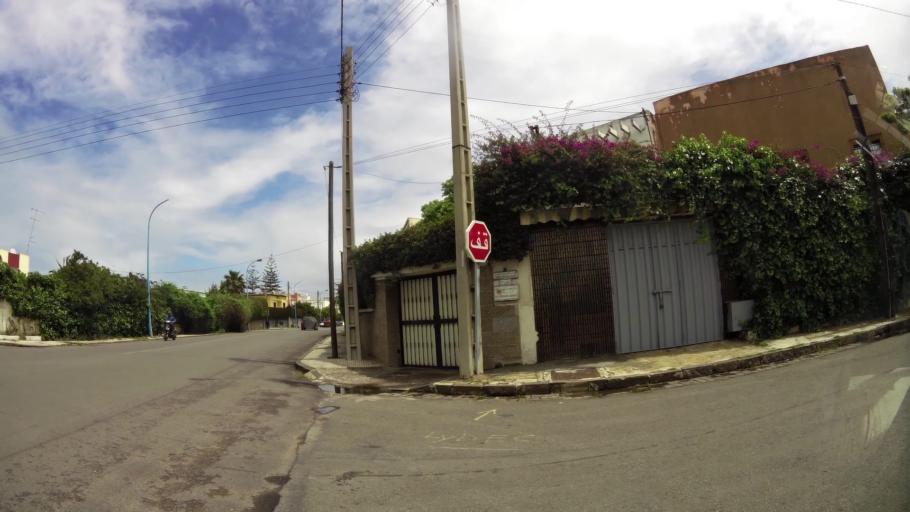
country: MA
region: Grand Casablanca
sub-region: Casablanca
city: Casablanca
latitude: 33.5650
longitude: -7.6322
